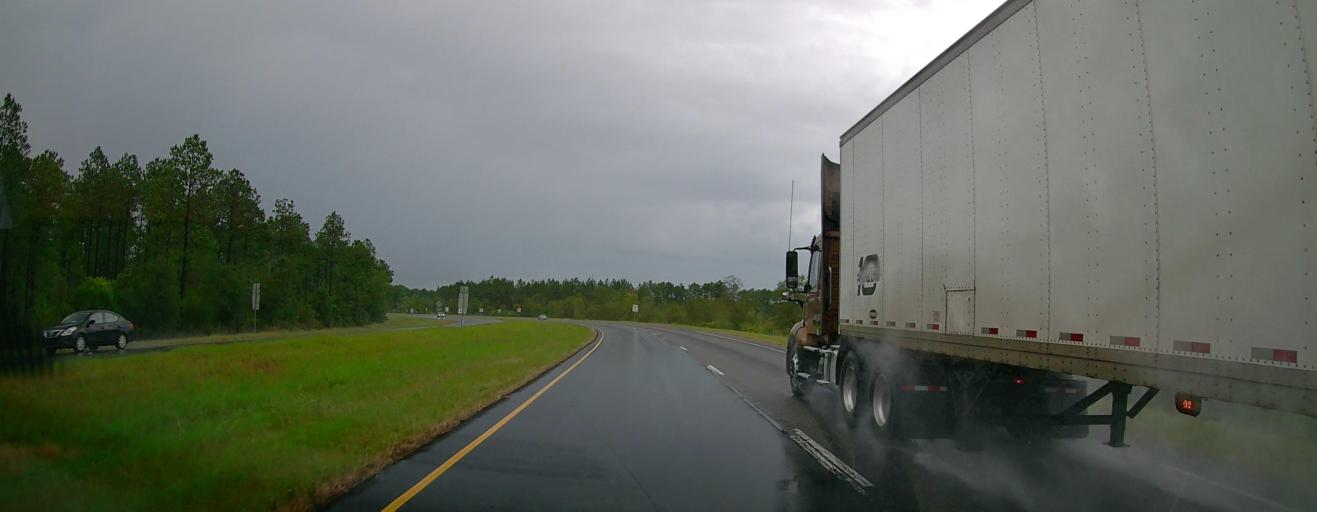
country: US
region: Georgia
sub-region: Ware County
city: Deenwood
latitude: 31.2111
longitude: -82.4162
